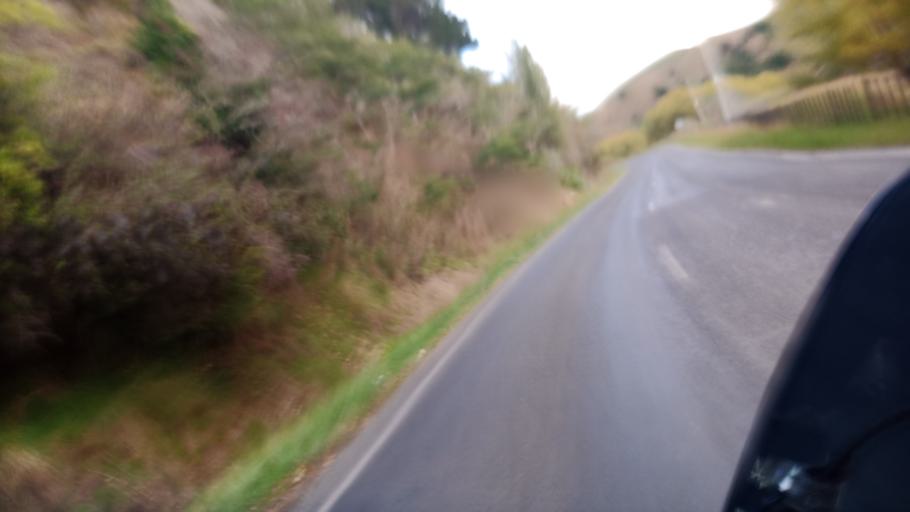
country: NZ
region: Gisborne
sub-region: Gisborne District
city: Gisborne
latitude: -38.5903
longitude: 177.7678
